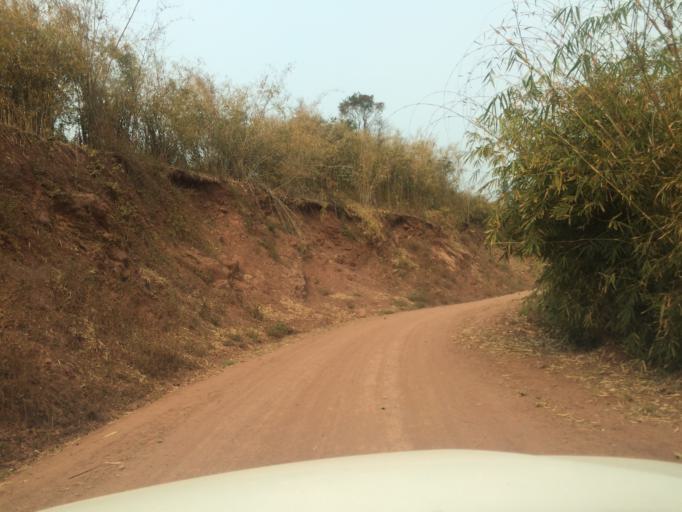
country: LA
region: Loungnamtha
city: Muang Nale
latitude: 20.4288
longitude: 101.7037
